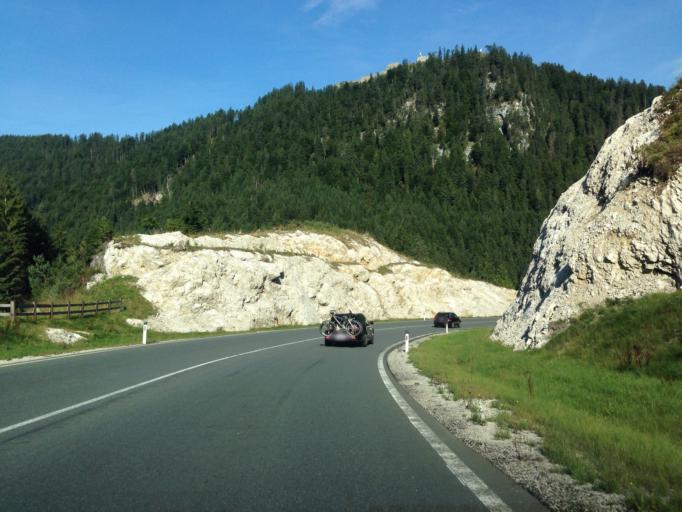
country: AT
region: Tyrol
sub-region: Politischer Bezirk Reutte
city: Ehenbichl
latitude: 47.4594
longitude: 10.7185
